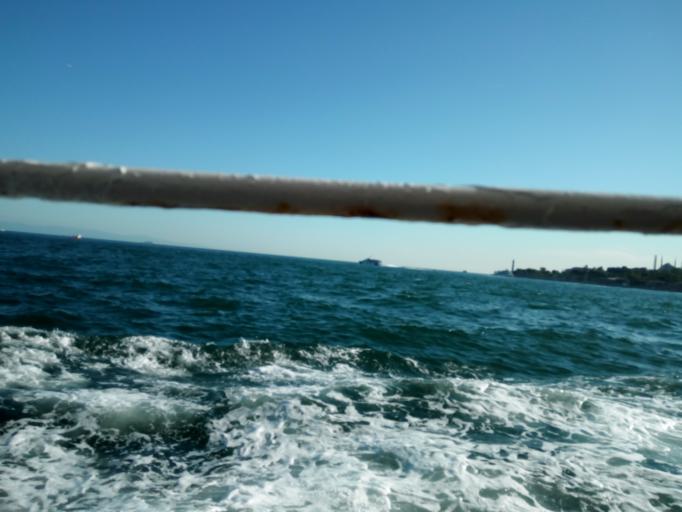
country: TR
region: Istanbul
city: Eminoenue
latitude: 41.0141
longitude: 28.9958
